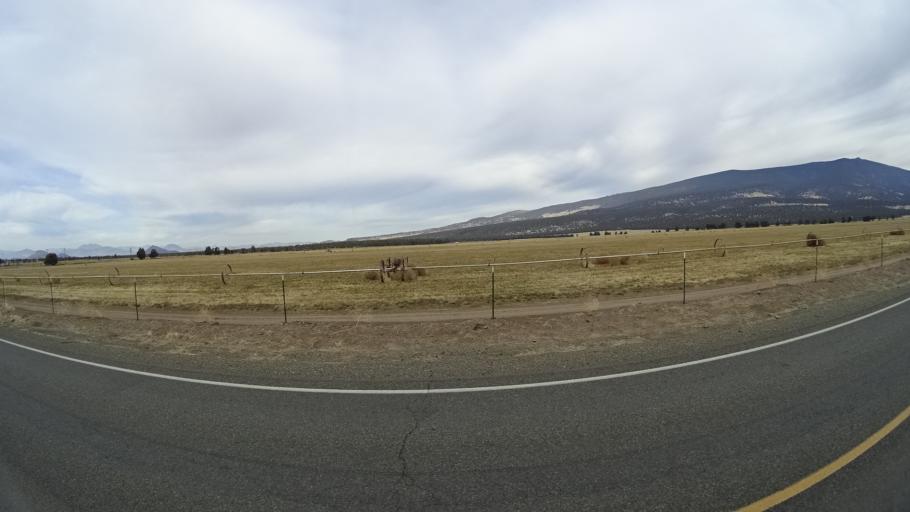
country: US
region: California
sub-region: Siskiyou County
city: Weed
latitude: 41.5953
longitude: -122.3287
